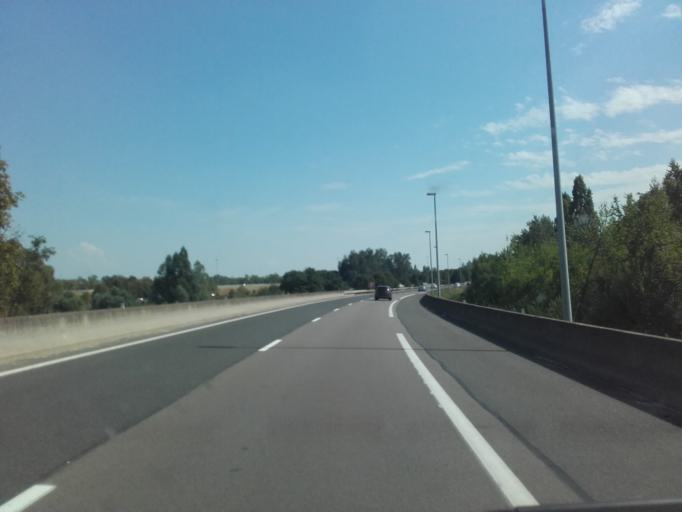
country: FR
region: Bourgogne
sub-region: Departement de la Cote-d'Or
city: Beaune
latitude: 47.0292
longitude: 4.8717
